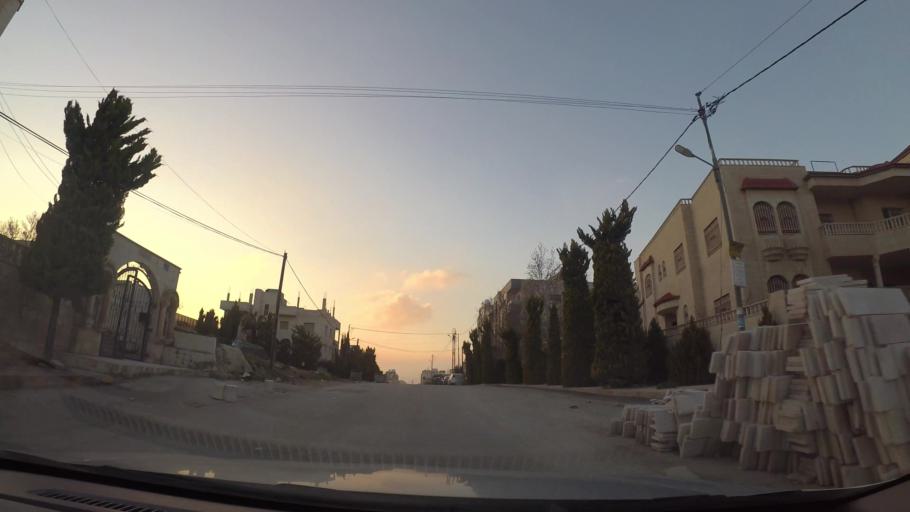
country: JO
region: Amman
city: Al Quwaysimah
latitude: 31.8984
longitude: 35.9299
